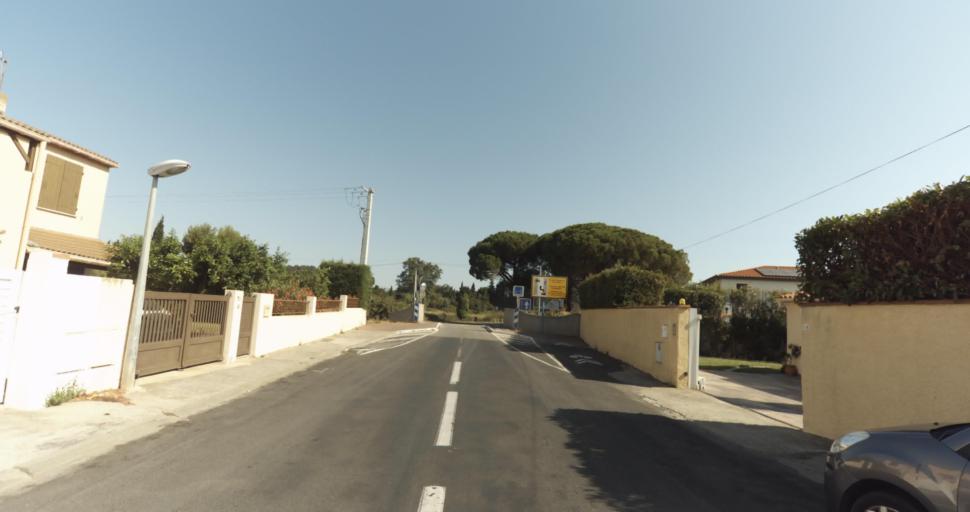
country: FR
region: Languedoc-Roussillon
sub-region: Departement des Pyrenees-Orientales
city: Latour-Bas-Elne
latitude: 42.6208
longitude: 3.0008
